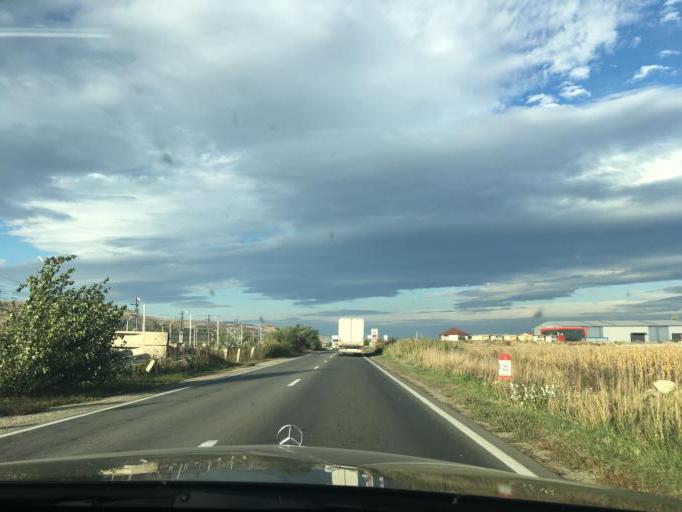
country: RO
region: Alba
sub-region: Municipiul Alba Iulia
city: Barabant
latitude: 46.0932
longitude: 23.6017
